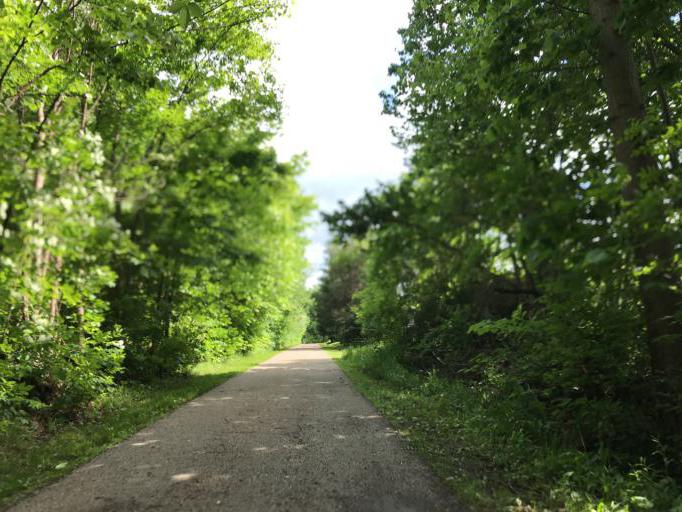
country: US
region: Michigan
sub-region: Oakland County
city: South Lyon
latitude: 42.4664
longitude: -83.6467
